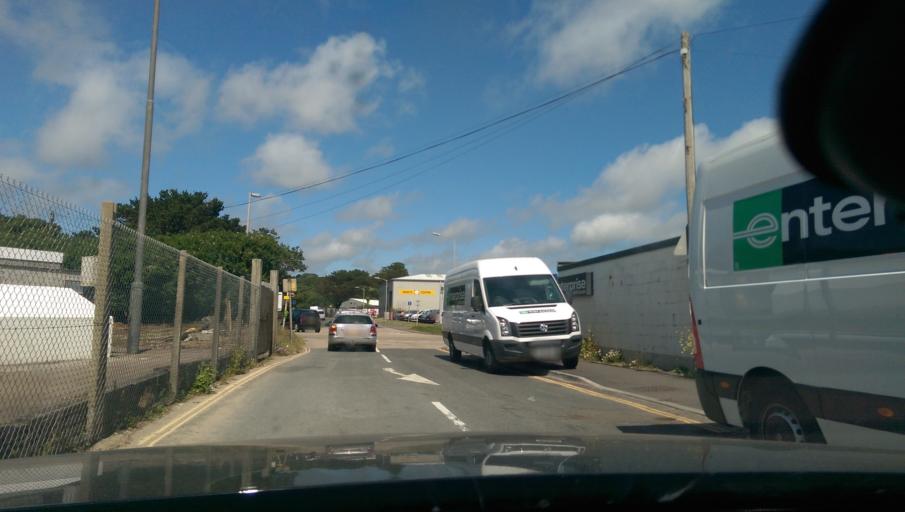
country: GB
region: England
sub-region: Cornwall
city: Marazion
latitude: 50.1285
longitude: -5.5027
